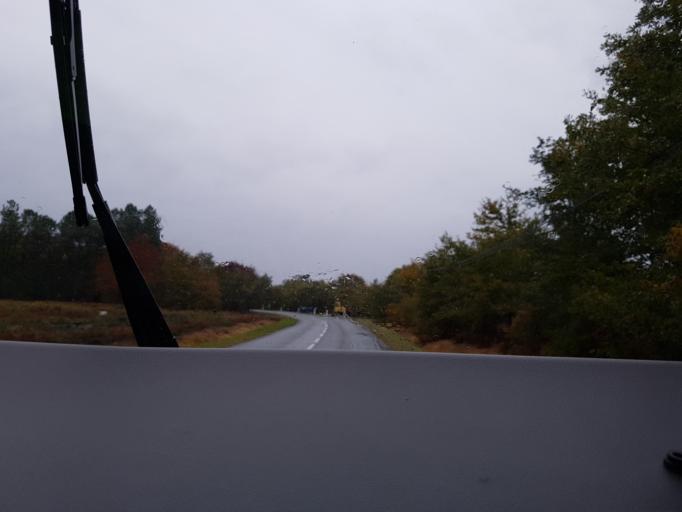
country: FR
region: Aquitaine
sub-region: Departement des Landes
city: Pissos
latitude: 44.3629
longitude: -0.6385
